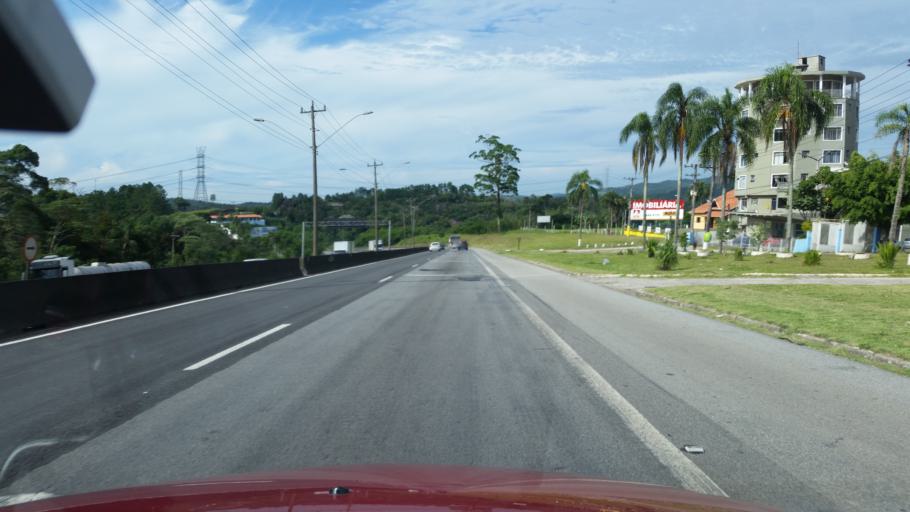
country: BR
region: Sao Paulo
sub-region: Sao Lourenco Da Serra
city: Sao Lourenco da Serra
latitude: -23.8053
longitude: -46.9227
